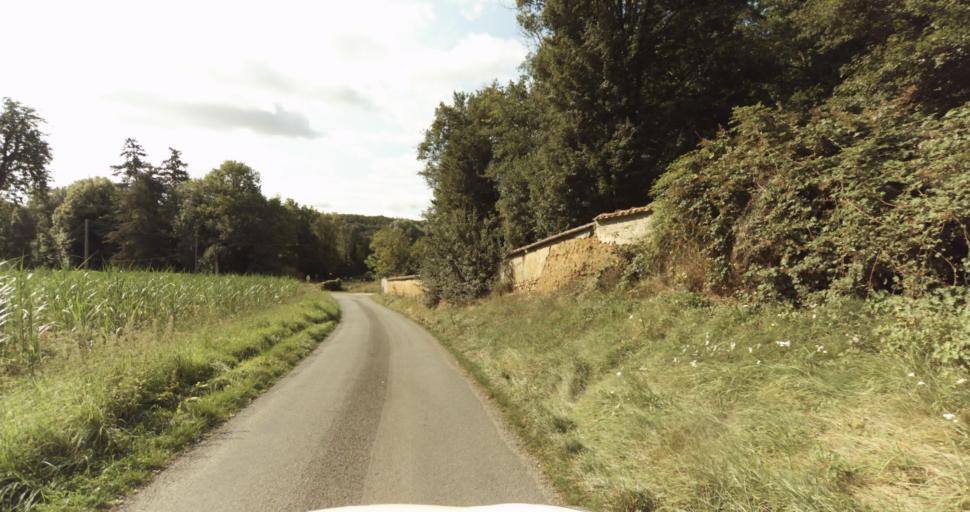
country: FR
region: Haute-Normandie
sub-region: Departement de l'Eure
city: Tillieres-sur-Avre
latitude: 48.7692
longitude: 1.1094
